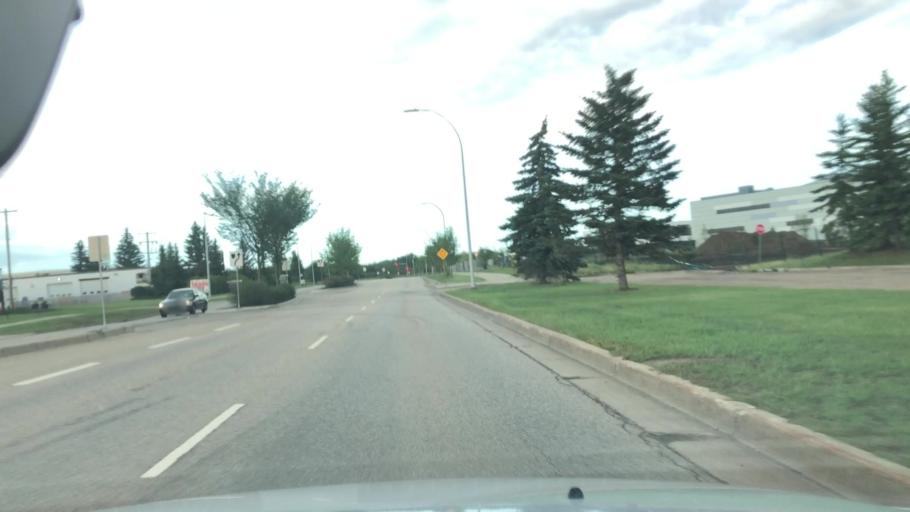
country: CA
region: Alberta
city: St. Albert
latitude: 53.6332
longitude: -113.5836
